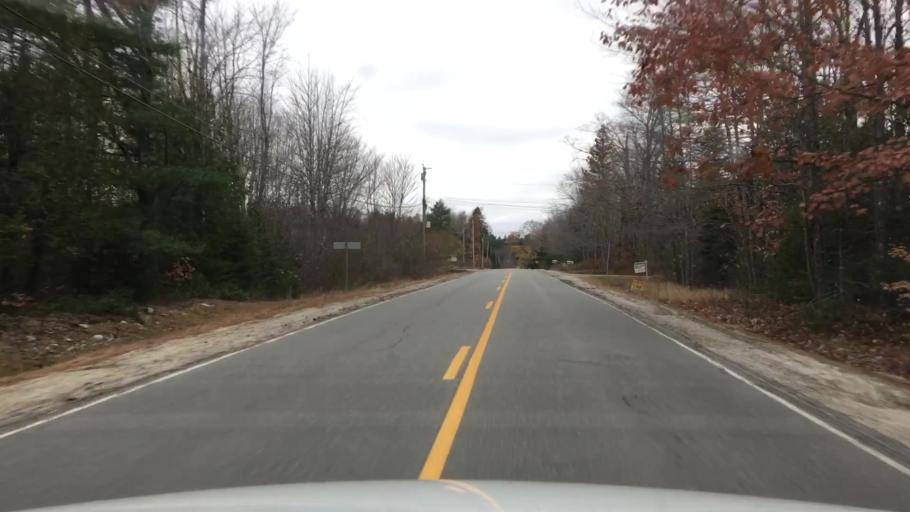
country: US
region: Maine
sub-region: Hancock County
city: Penobscot
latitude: 44.4202
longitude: -68.6176
